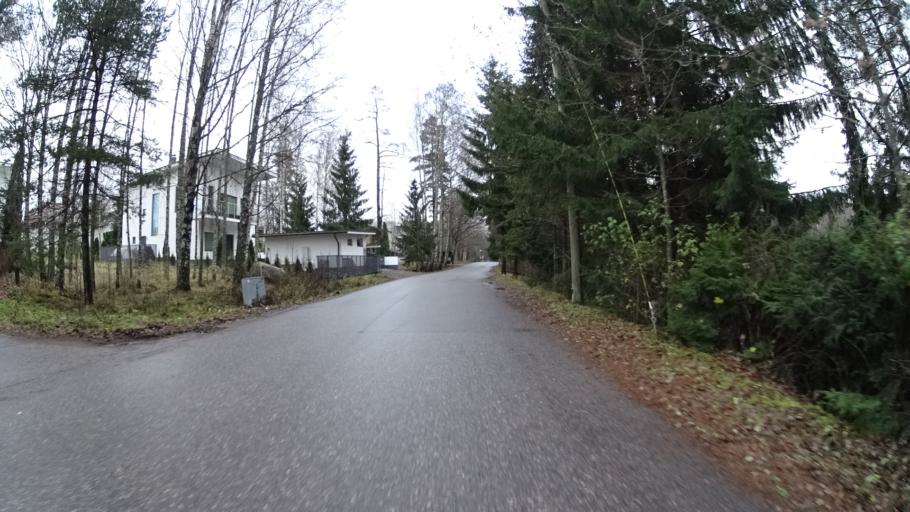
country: FI
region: Uusimaa
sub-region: Helsinki
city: Kauniainen
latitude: 60.2228
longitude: 24.7029
